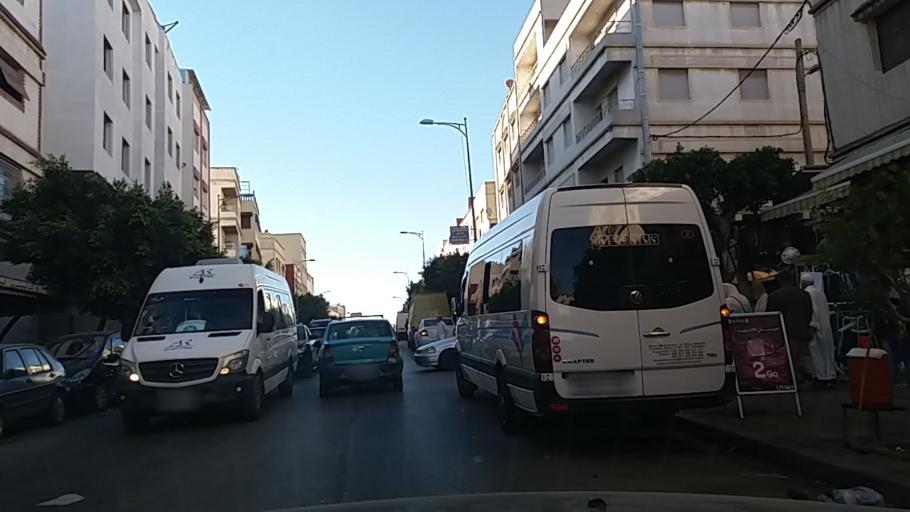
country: MA
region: Tanger-Tetouan
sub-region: Tanger-Assilah
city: Tangier
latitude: 35.7546
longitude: -5.8204
